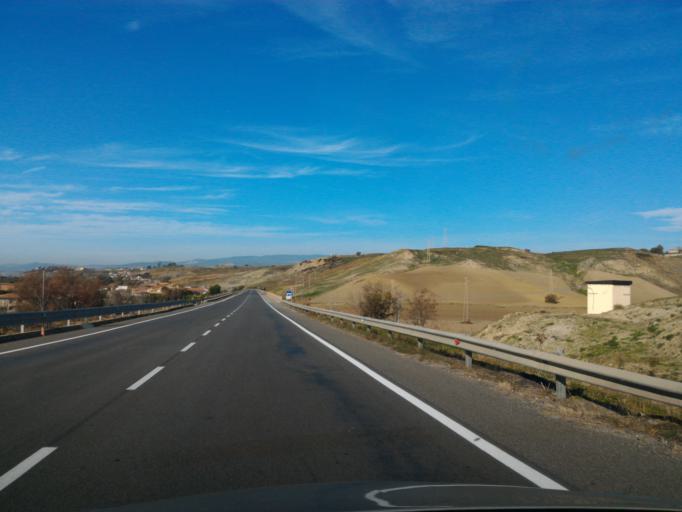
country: IT
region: Calabria
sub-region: Provincia di Crotone
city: Le Castella
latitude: 38.9386
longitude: 16.9886
